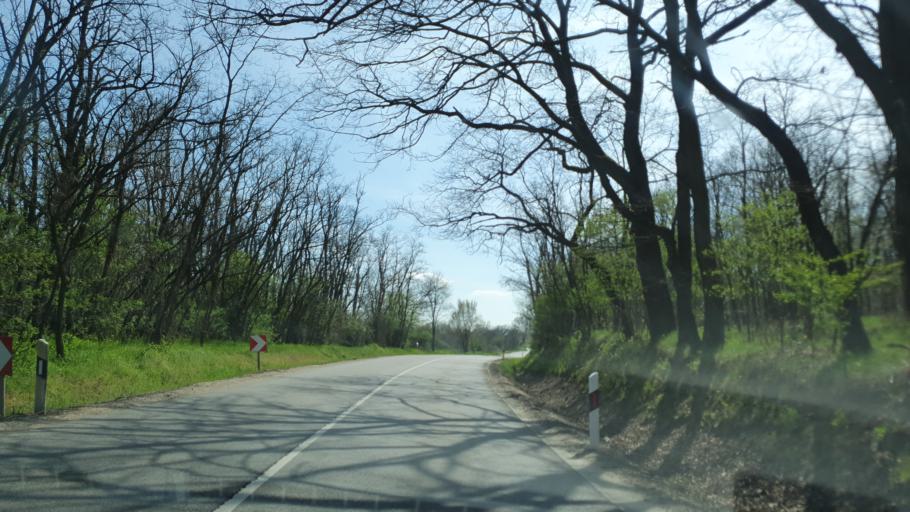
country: HU
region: Fejer
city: Pusztavam
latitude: 47.4535
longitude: 18.2403
